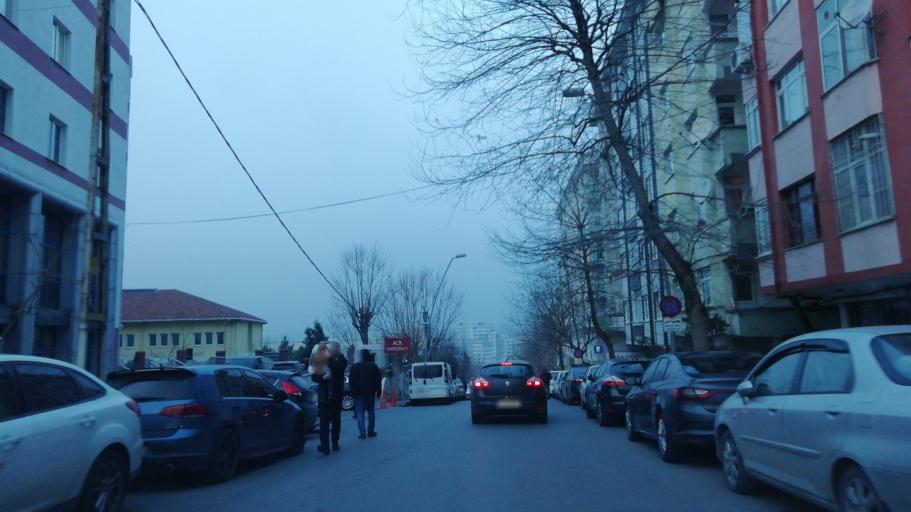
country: TR
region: Istanbul
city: Bahcelievler
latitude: 40.9993
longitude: 28.8298
